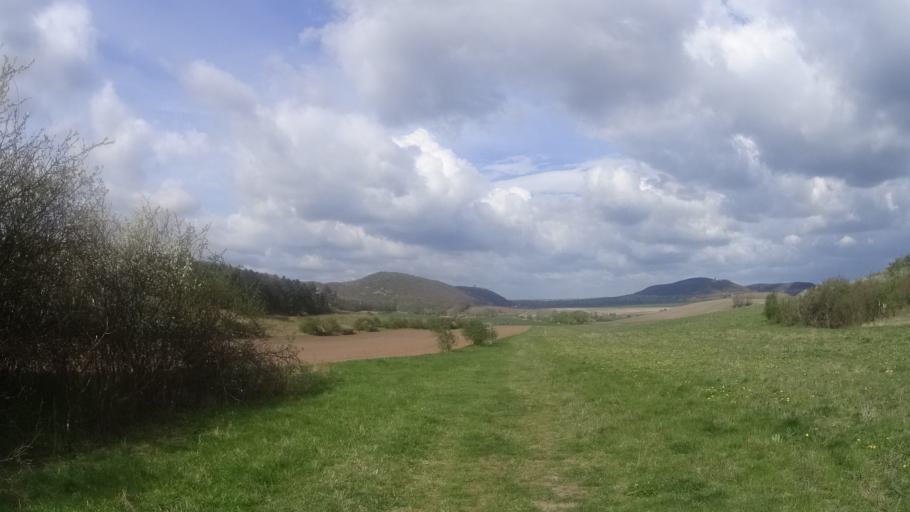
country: DE
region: Thuringia
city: Wandersleben
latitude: 50.8613
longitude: 10.8714
